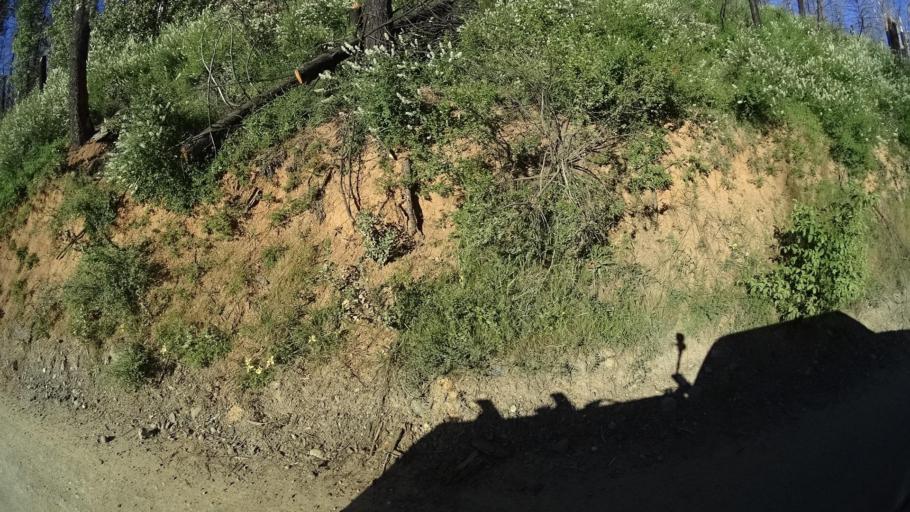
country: US
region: California
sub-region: Lake County
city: Upper Lake
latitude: 39.3410
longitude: -122.9595
